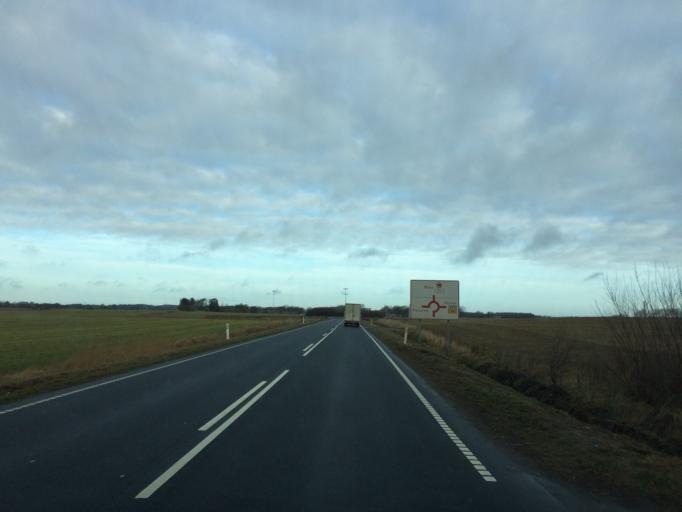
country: DK
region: Central Jutland
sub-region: Struer Kommune
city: Struer
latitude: 56.4655
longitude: 8.5465
